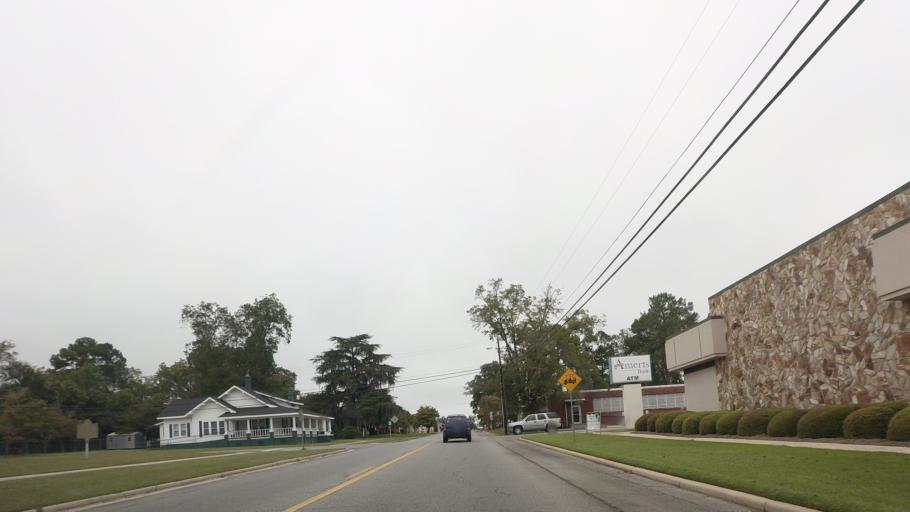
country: US
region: Georgia
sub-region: Irwin County
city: Ocilla
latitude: 31.5919
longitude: -83.2506
